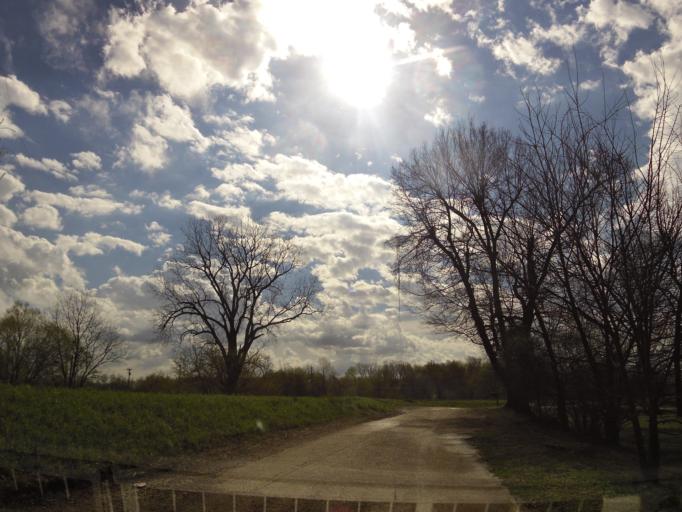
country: US
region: Missouri
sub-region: Butler County
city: Poplar Bluff
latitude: 36.7635
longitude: -90.3799
